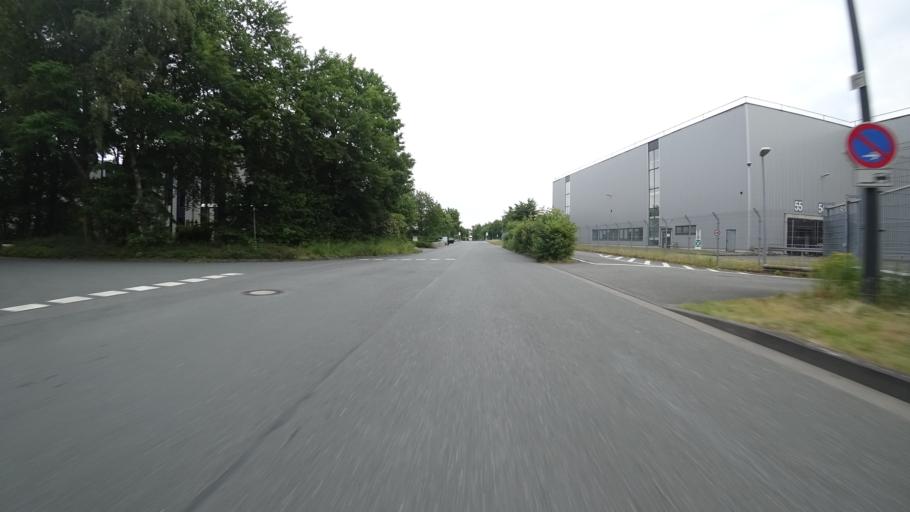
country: DE
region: North Rhine-Westphalia
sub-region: Regierungsbezirk Detmold
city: Verl
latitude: 51.8862
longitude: 8.4473
